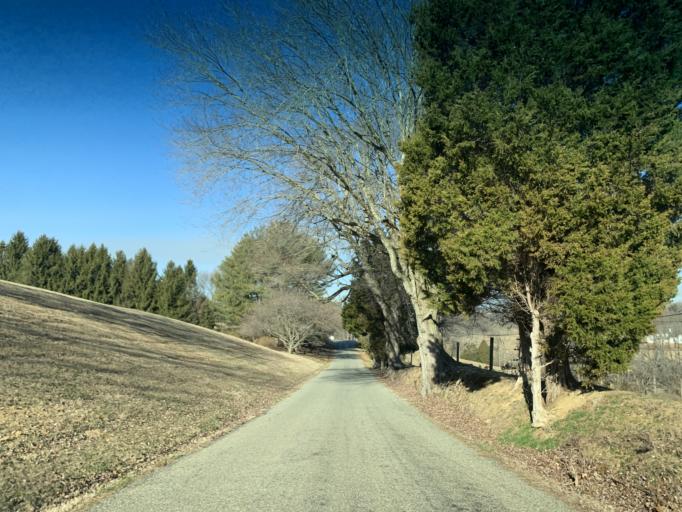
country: US
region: Maryland
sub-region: Harford County
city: Aberdeen
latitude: 39.6092
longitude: -76.2104
